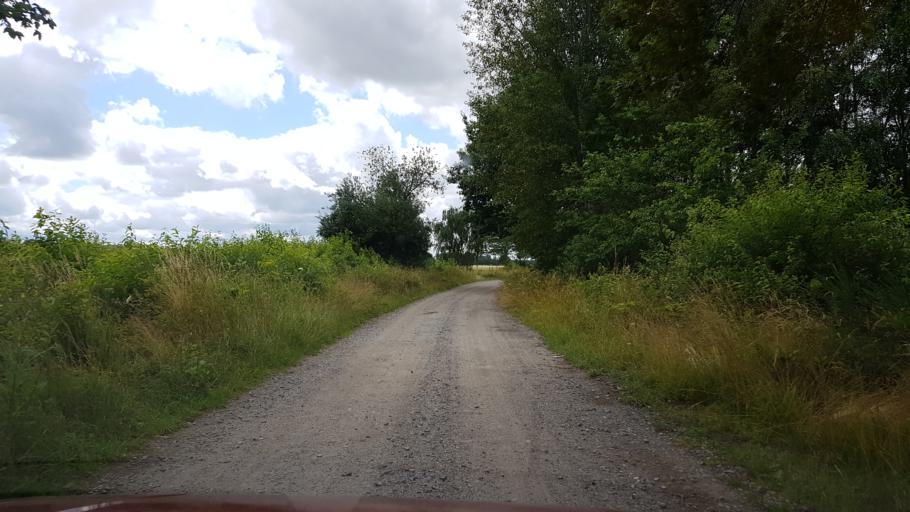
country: PL
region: West Pomeranian Voivodeship
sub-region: Powiat bialogardzki
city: Karlino
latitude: 54.1649
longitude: 15.9420
